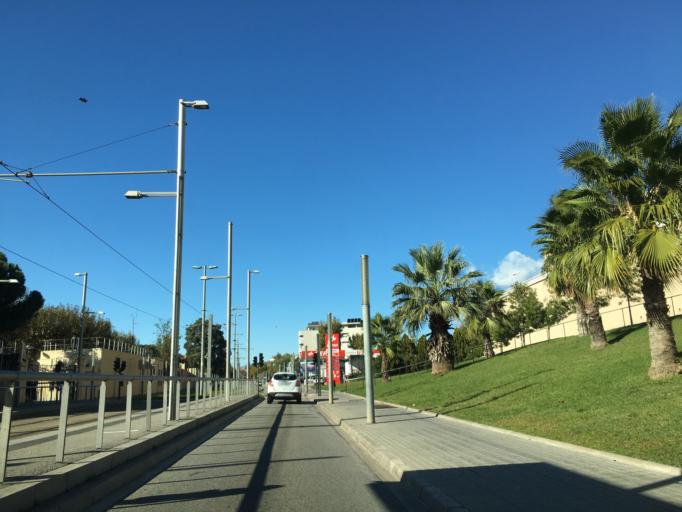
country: ES
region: Catalonia
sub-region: Provincia de Barcelona
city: Sant Joan Despi
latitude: 41.3567
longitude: 2.0662
